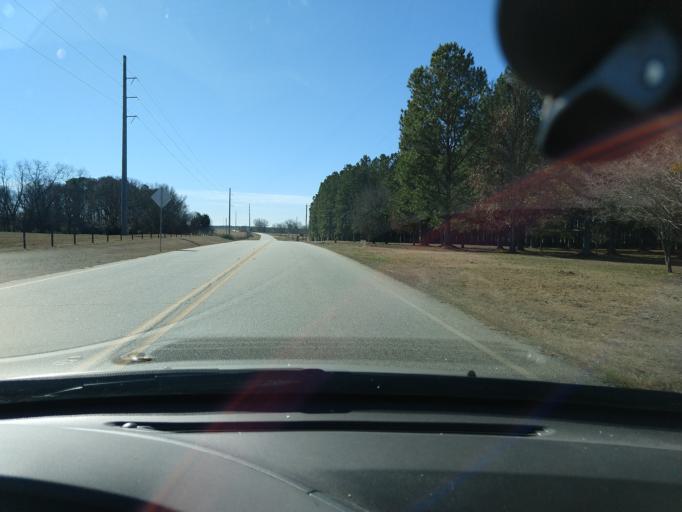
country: US
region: Georgia
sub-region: Walton County
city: Social Circle
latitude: 33.5081
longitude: -83.7350
